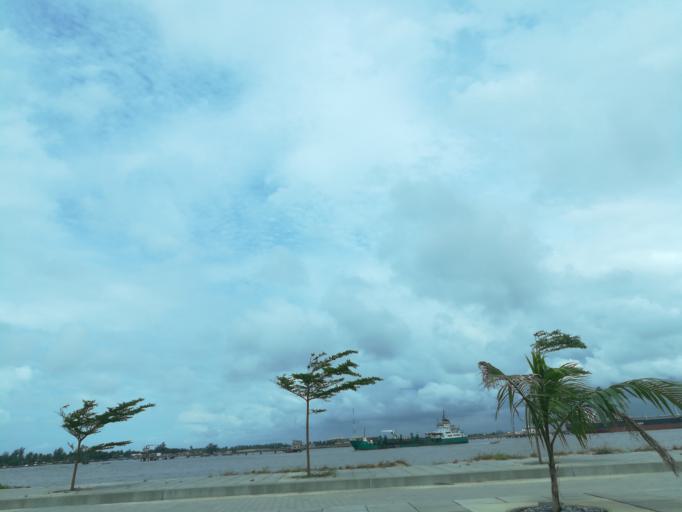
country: NG
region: Lagos
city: Lagos
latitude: 6.4084
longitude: 3.4032
